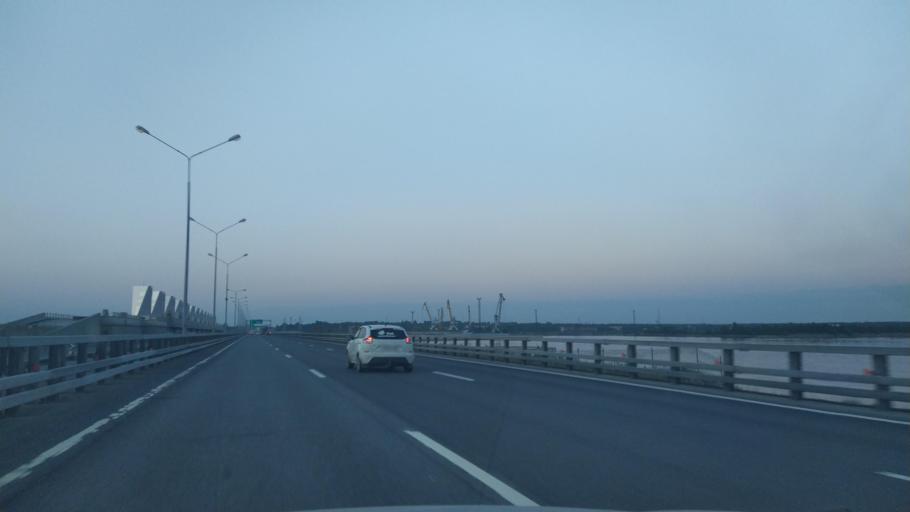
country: RU
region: Leningrad
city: Gorskaya
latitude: 60.0363
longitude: 29.9467
